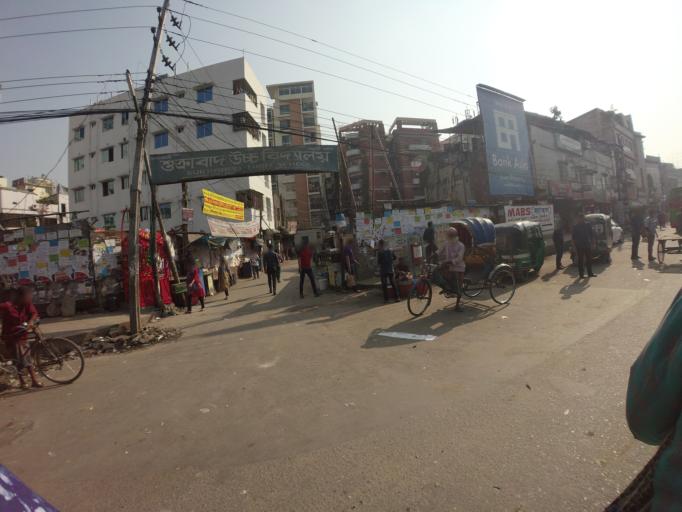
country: BD
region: Dhaka
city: Azimpur
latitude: 23.7524
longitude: 90.3777
